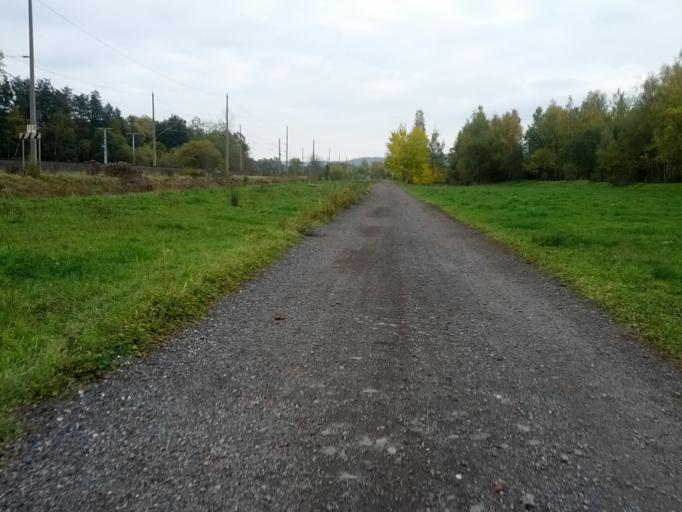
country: DE
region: Thuringia
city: Seebach
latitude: 50.9499
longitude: 10.4157
